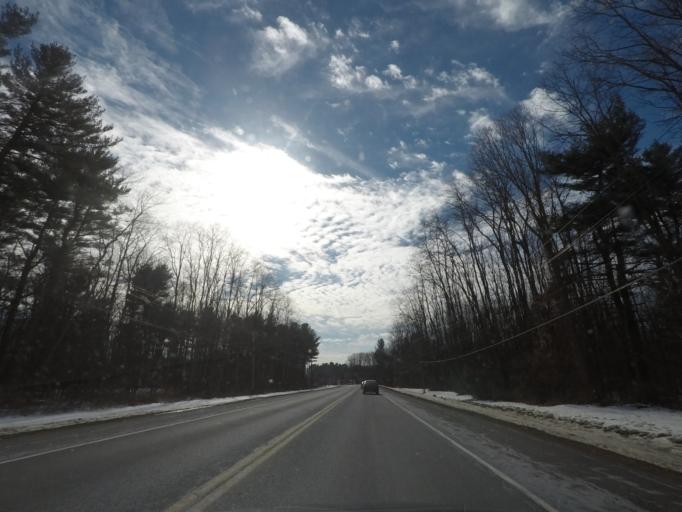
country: US
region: New York
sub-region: Albany County
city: Westmere
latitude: 42.7057
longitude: -73.8803
